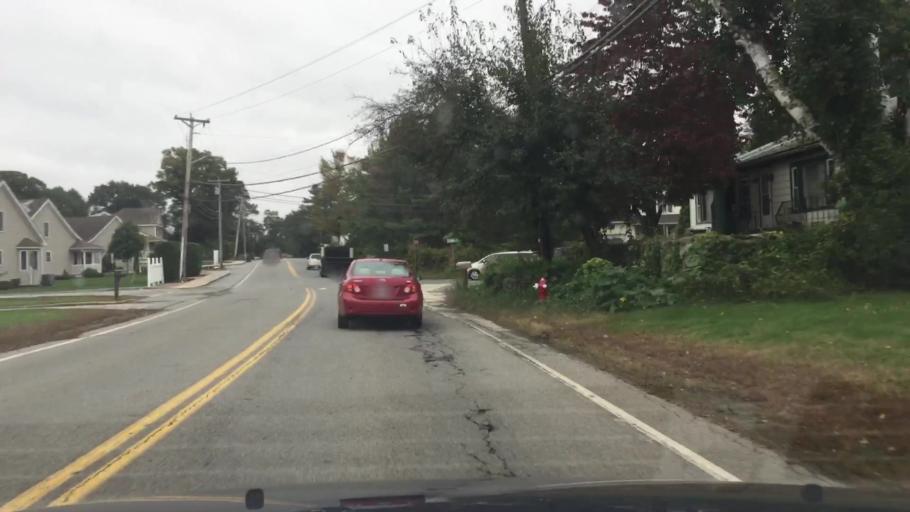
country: US
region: Massachusetts
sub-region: Middlesex County
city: Tyngsboro
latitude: 42.6822
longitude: -71.3693
